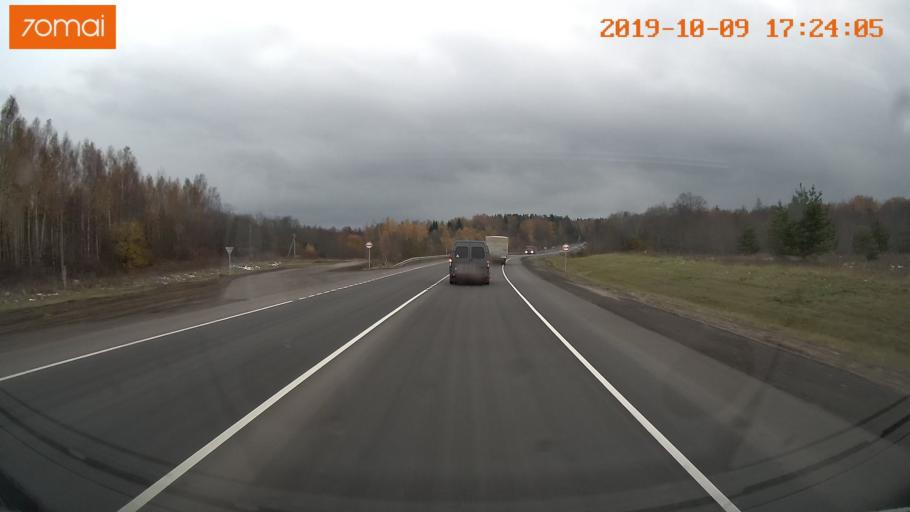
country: RU
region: Ivanovo
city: Furmanov
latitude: 57.1885
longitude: 41.1117
